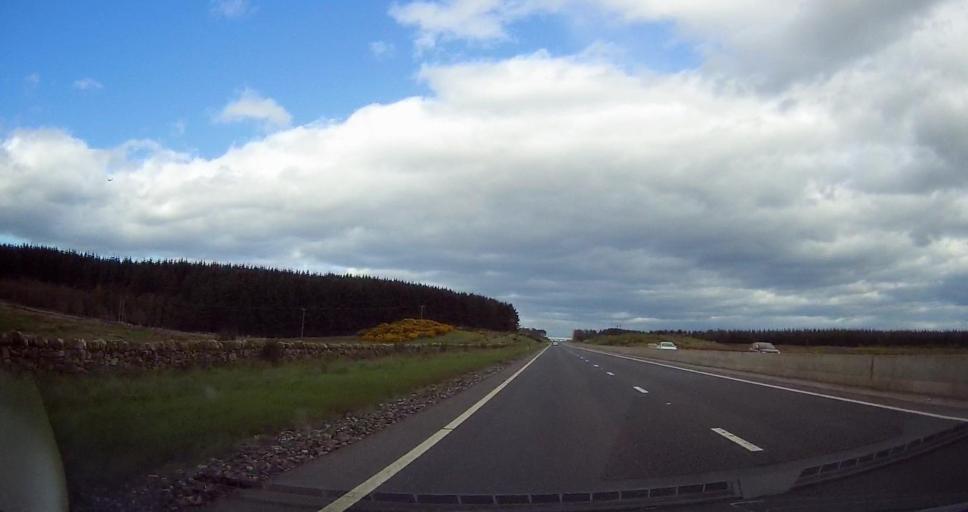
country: GB
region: Scotland
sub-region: Aberdeenshire
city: Portlethen
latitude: 57.0868
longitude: -2.1387
